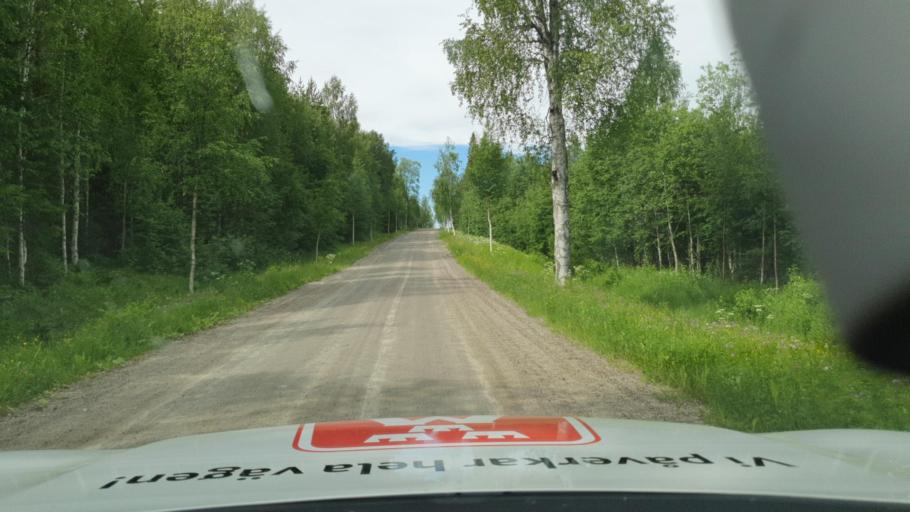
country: SE
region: Vaesterbotten
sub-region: Skelleftea Kommun
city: Burtraesk
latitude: 64.4726
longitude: 20.4504
